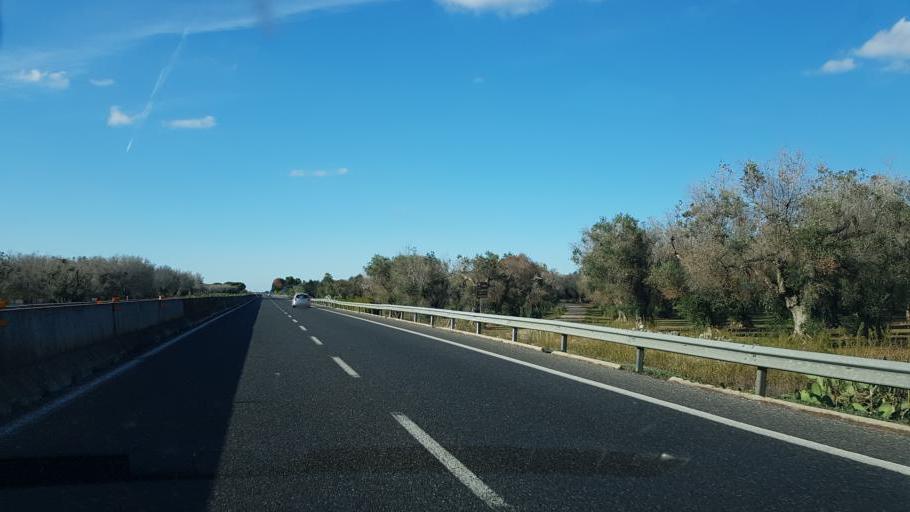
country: IT
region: Apulia
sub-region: Provincia di Brindisi
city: Torchiarolo
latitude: 40.4708
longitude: 18.0509
